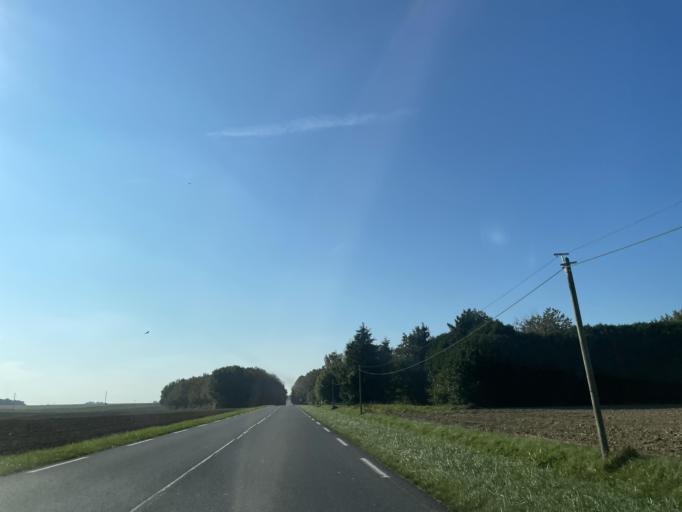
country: FR
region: Ile-de-France
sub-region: Departement de Seine-et-Marne
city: Chailly-en-Brie
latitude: 48.7878
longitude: 3.1560
